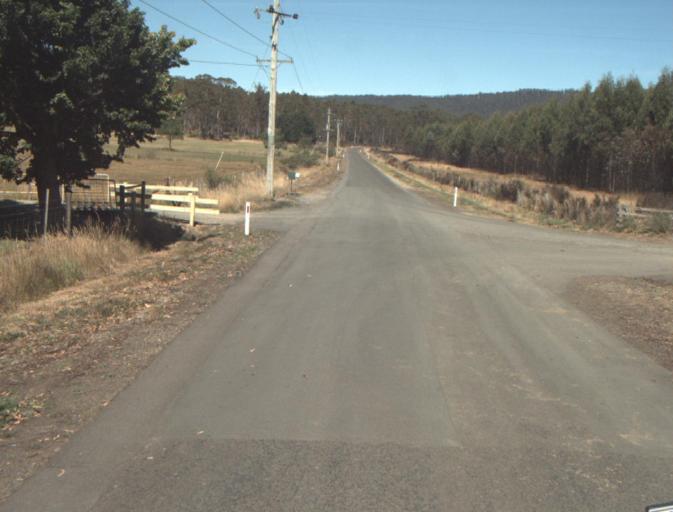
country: AU
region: Tasmania
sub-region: Launceston
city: Newstead
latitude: -41.3222
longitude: 147.3214
